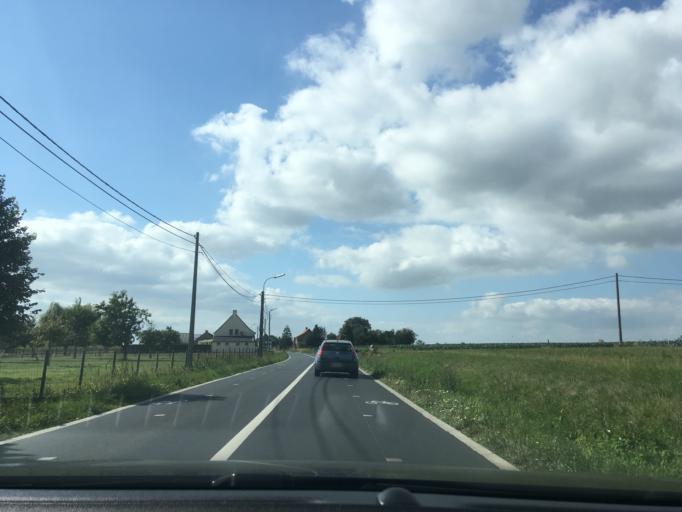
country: BE
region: Flanders
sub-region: Provincie West-Vlaanderen
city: Moorslede
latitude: 50.9146
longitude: 3.0289
